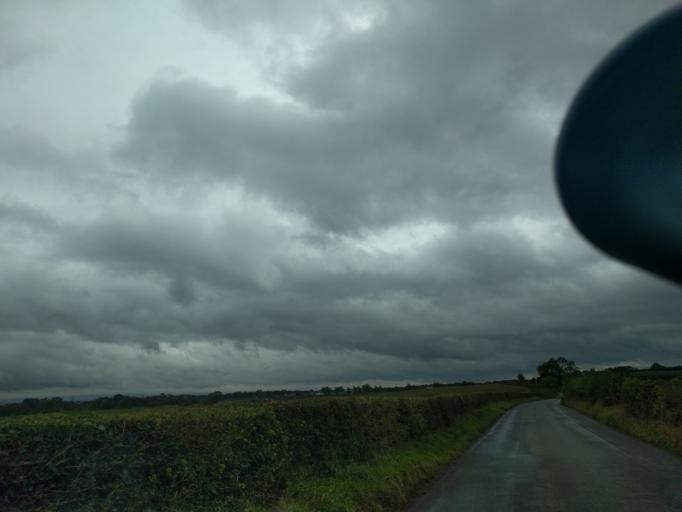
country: GB
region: England
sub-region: North Yorkshire
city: Bedale
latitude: 54.3409
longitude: -1.5834
